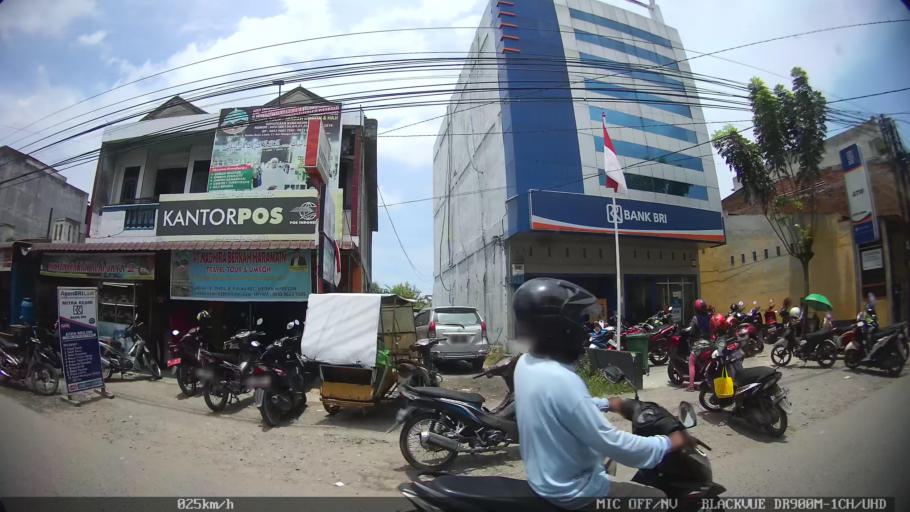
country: ID
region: North Sumatra
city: Labuhan Deli
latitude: 3.6884
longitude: 98.6615
